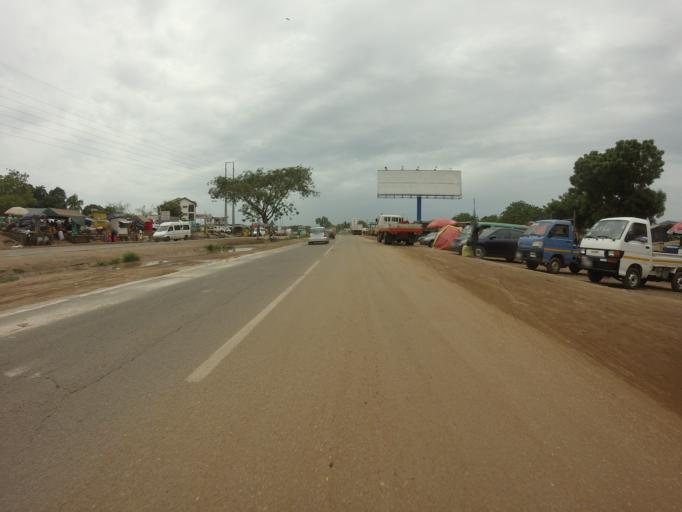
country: GH
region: Greater Accra
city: Achiaman
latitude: 5.7060
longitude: -0.2983
